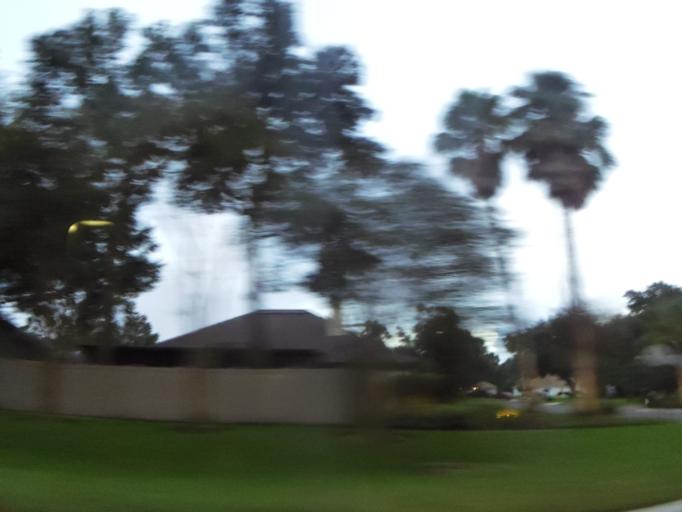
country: US
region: Florida
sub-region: Duval County
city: Jacksonville
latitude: 30.3812
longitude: -81.6109
